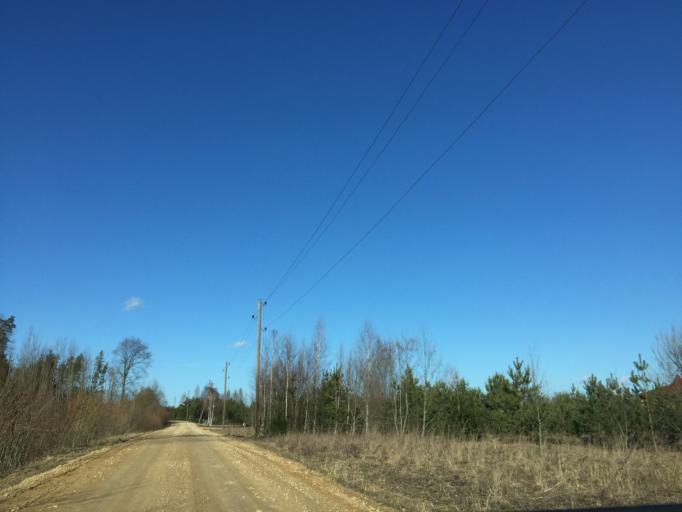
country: LV
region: Ogre
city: Ogre
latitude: 56.8756
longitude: 24.7088
